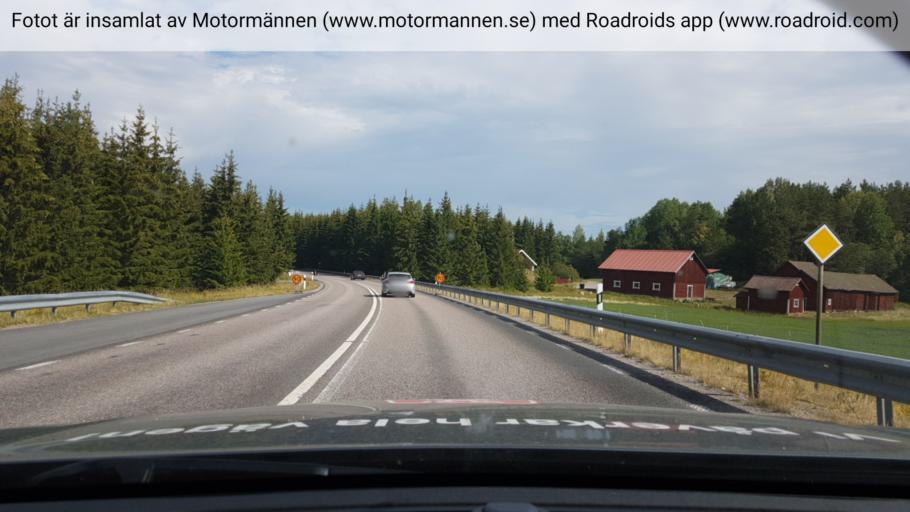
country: SE
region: Uppsala
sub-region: Enkopings Kommun
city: Orsundsbro
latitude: 59.8592
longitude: 17.3733
